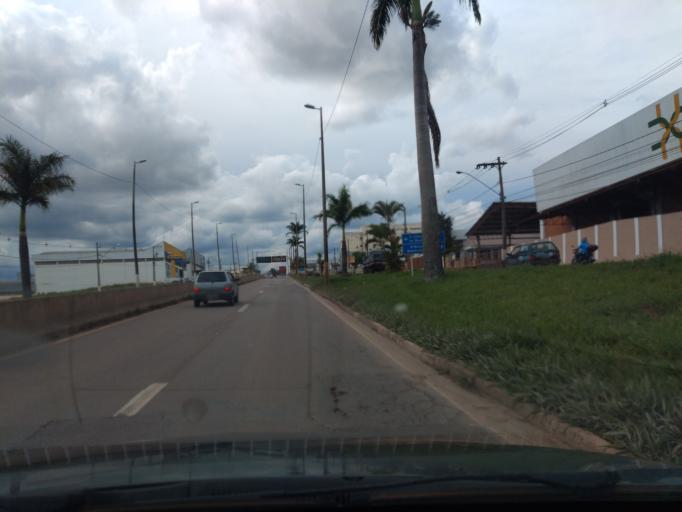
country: BR
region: Minas Gerais
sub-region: Varginha
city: Varginha
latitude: -21.5862
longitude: -45.4387
